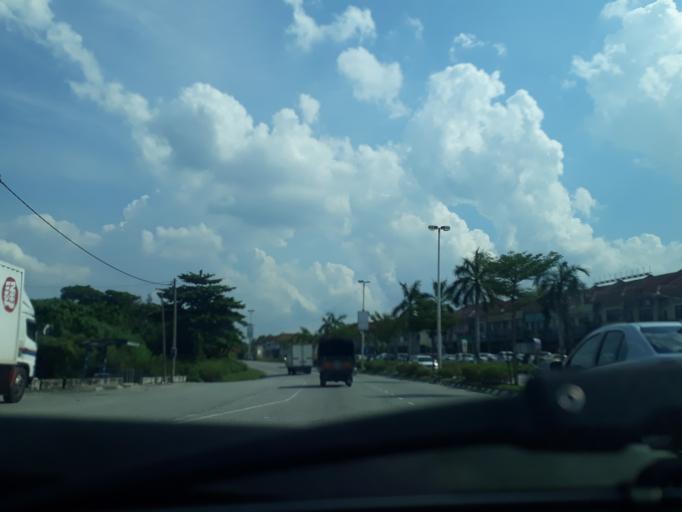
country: MY
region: Perak
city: Ipoh
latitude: 4.6407
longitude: 101.0941
